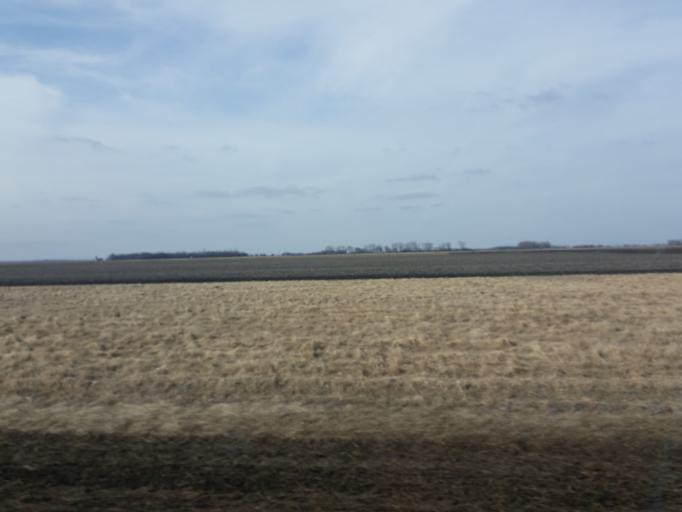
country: US
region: Minnesota
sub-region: Clay County
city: Barnesville
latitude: 46.4711
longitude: -96.4152
